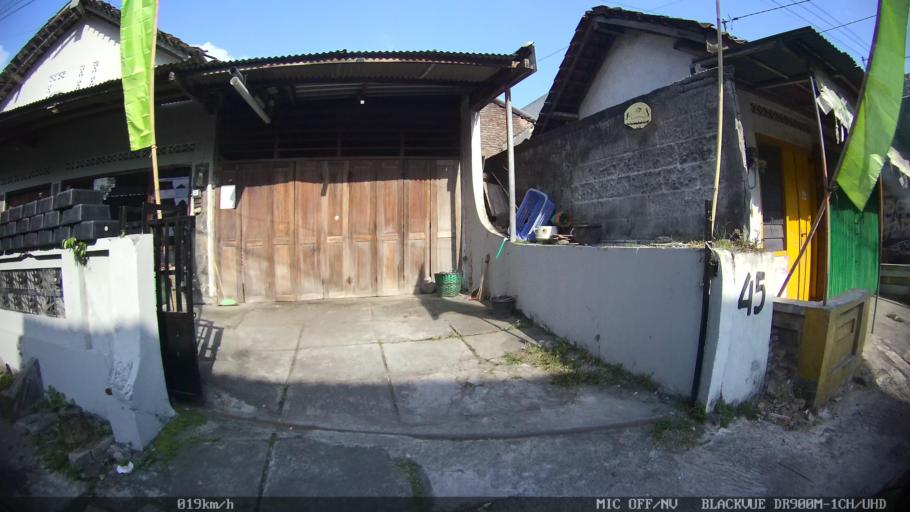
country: ID
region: Daerah Istimewa Yogyakarta
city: Yogyakarta
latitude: -7.7994
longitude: 110.3486
